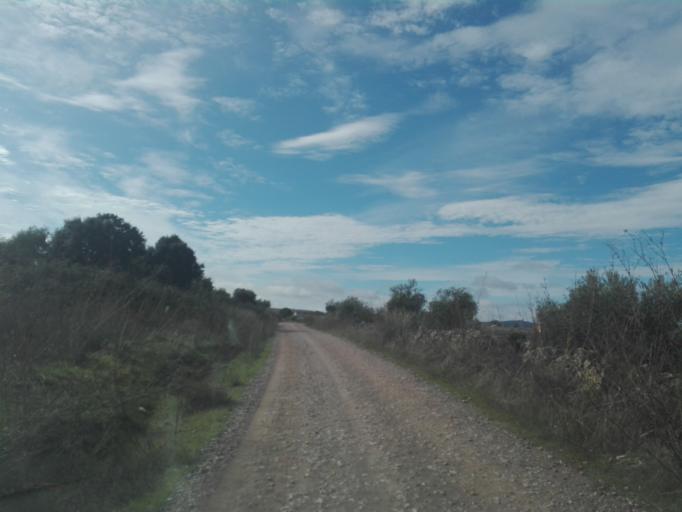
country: ES
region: Extremadura
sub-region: Provincia de Badajoz
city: Villagarcia de la Torre
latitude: 38.3067
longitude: -6.0835
